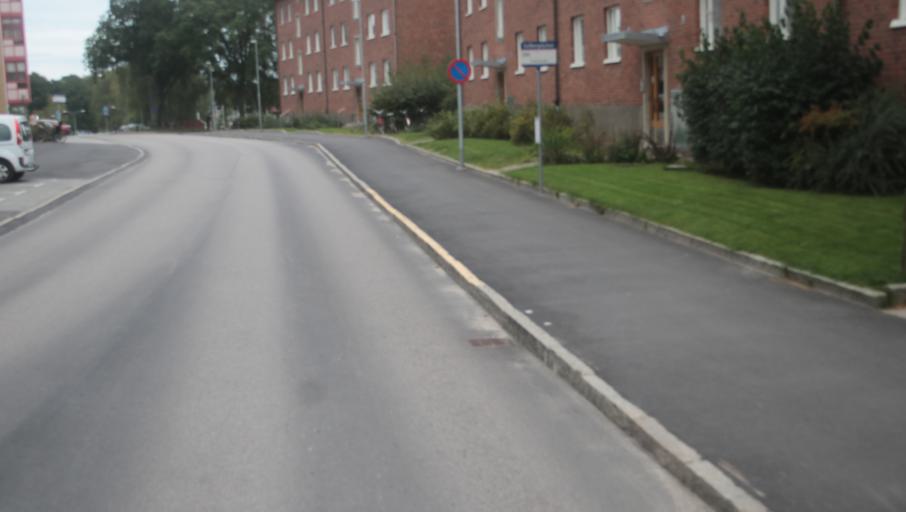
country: SE
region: Blekinge
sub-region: Karlshamns Kommun
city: Karlshamn
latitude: 56.1659
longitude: 14.8776
